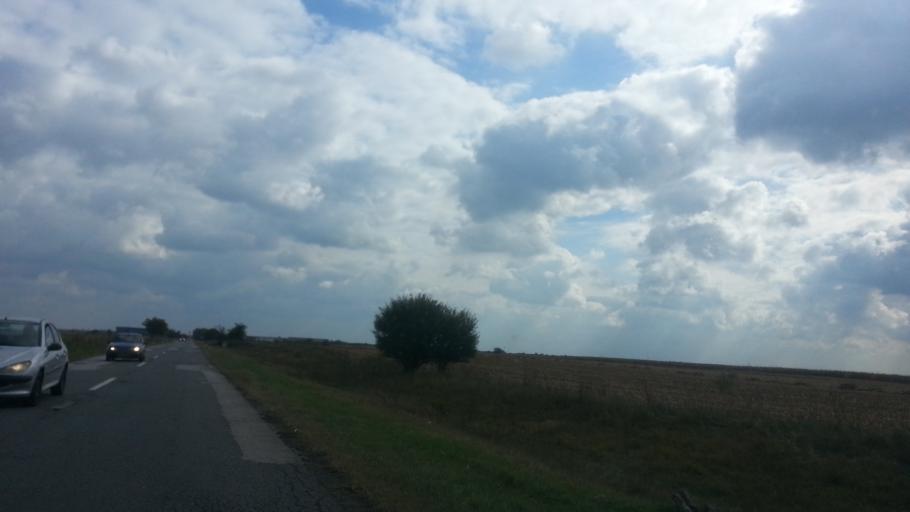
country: RS
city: Stari Banovci
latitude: 44.9864
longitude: 20.2447
